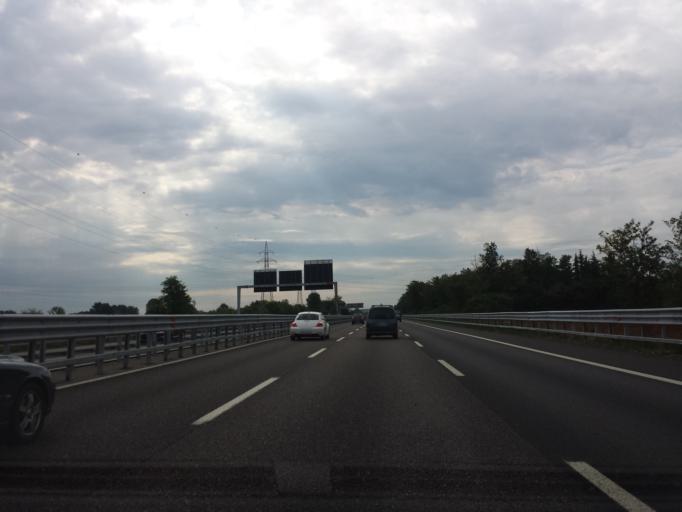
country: IT
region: Lombardy
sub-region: Citta metropolitana di Milano
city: Figino
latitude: 45.4814
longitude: 9.0726
